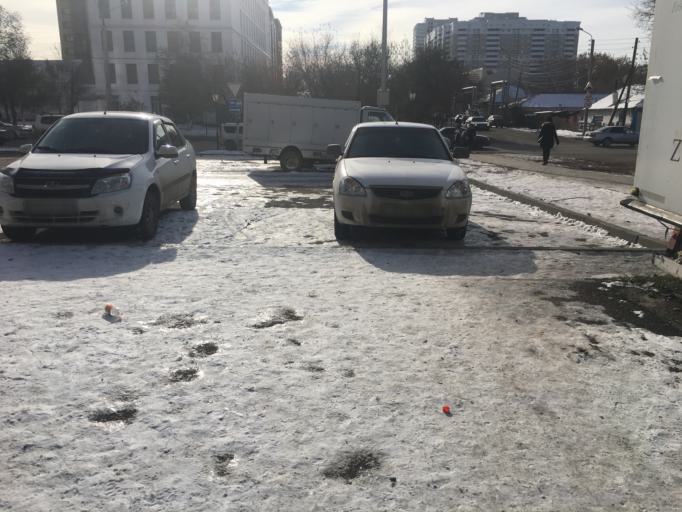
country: KZ
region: Astana Qalasy
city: Astana
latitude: 51.1679
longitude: 71.4445
